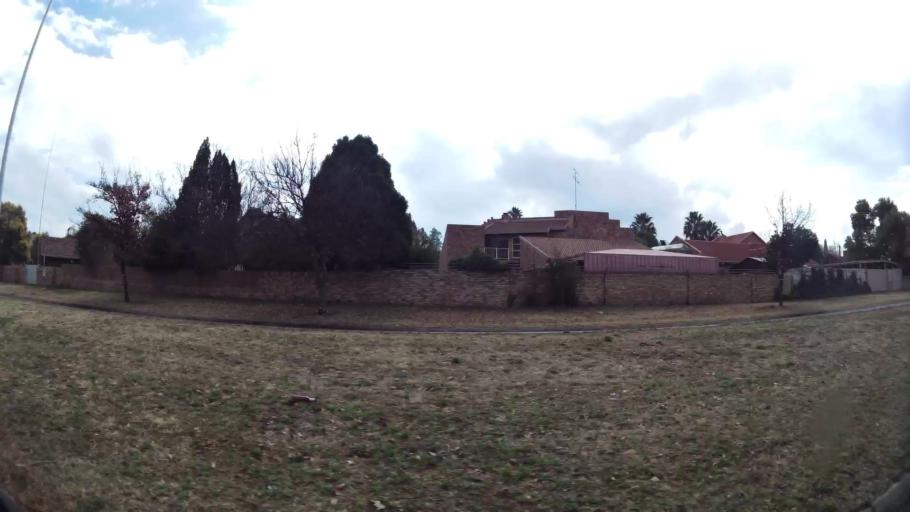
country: ZA
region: Gauteng
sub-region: Sedibeng District Municipality
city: Vanderbijlpark
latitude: -26.7433
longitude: 27.8480
